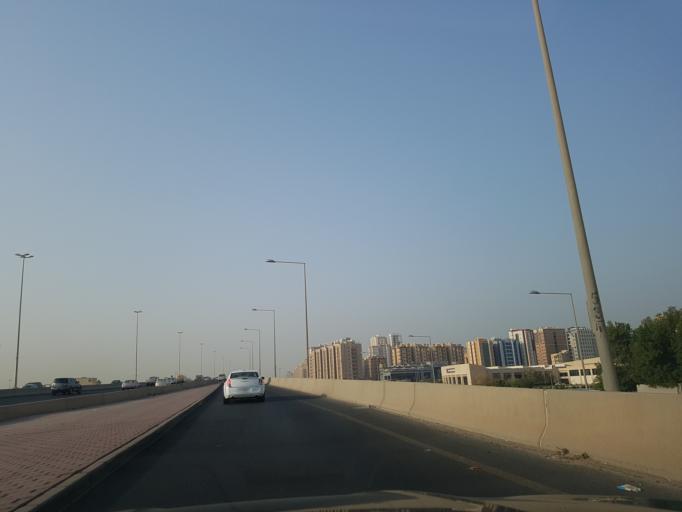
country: KW
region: Al Ahmadi
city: Al Mahbulah
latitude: 29.1331
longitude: 48.1152
